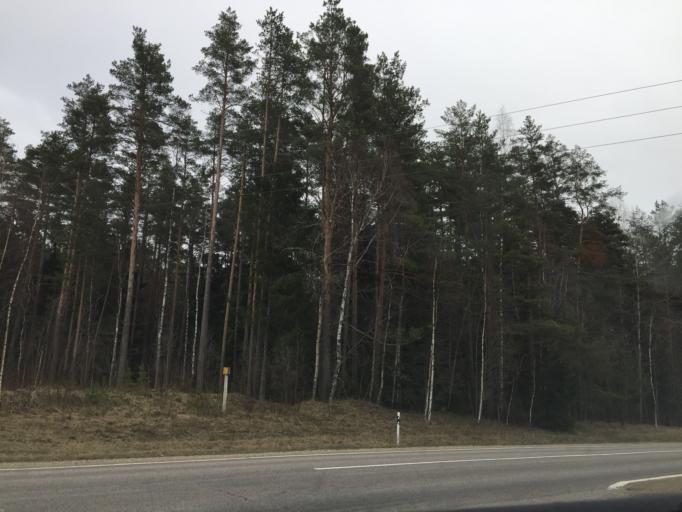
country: LV
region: Kraslavas Rajons
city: Kraslava
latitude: 55.9133
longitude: 26.9974
